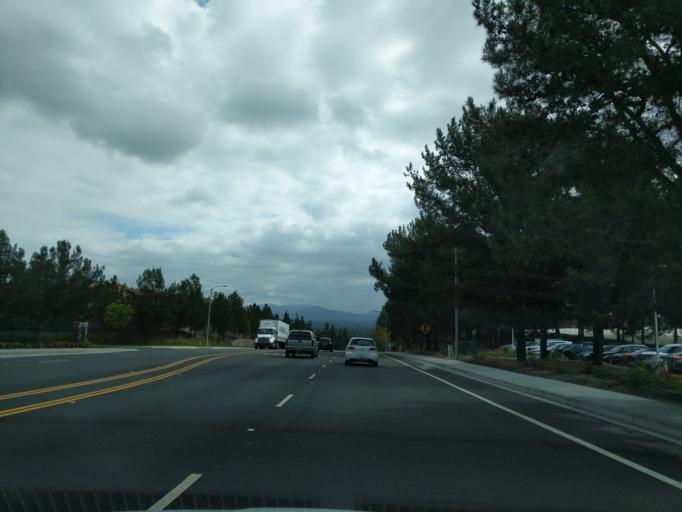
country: US
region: California
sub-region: Orange County
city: Laguna Woods
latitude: 33.5951
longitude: -117.7247
